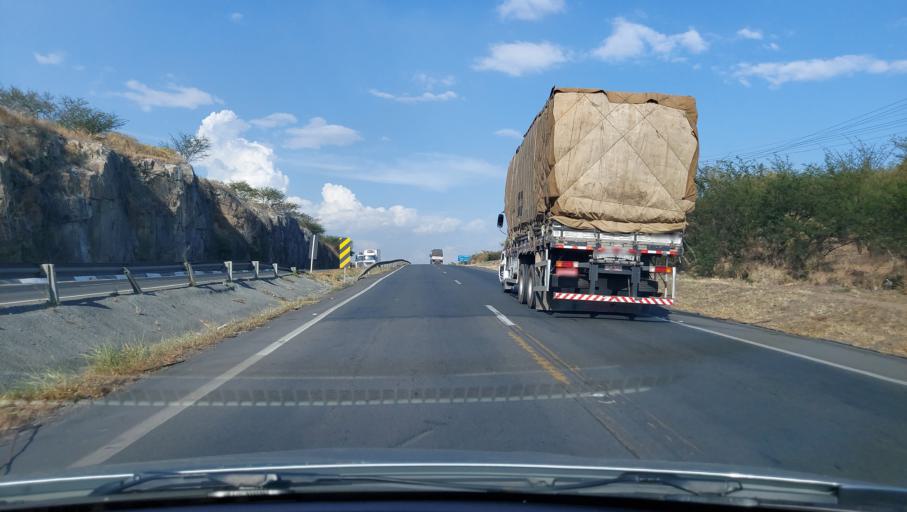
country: BR
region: Bahia
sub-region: Santo Estevao
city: Santo Estevao
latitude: -12.4277
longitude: -39.2095
